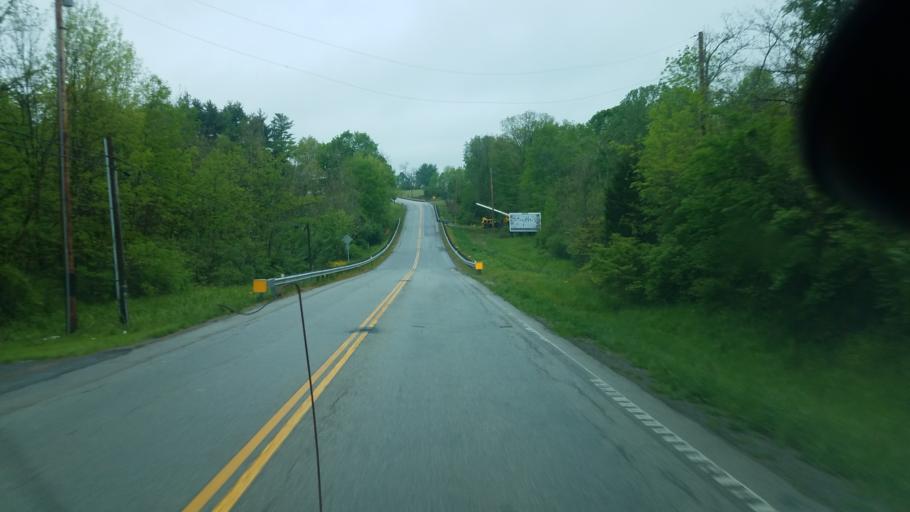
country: US
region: Ohio
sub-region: Highland County
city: Hillsboro
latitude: 39.2516
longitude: -83.6029
